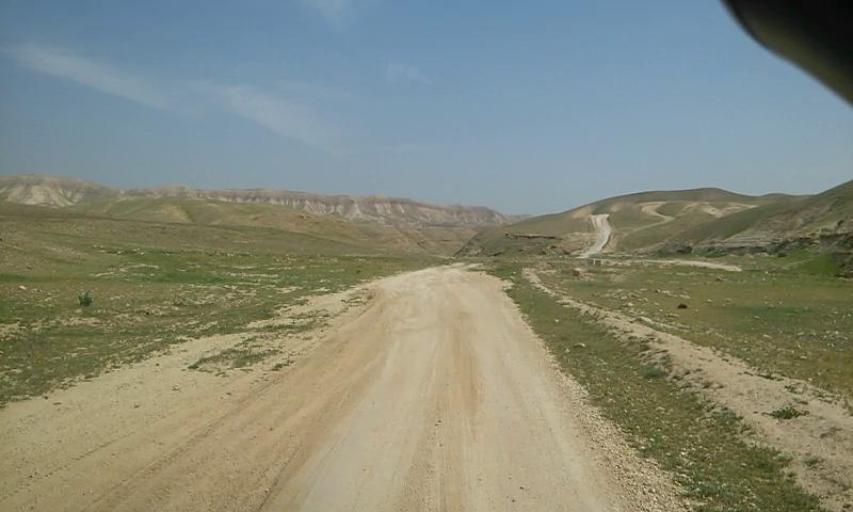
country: PS
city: `Arab ar Rashaydah
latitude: 31.5054
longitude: 35.2897
